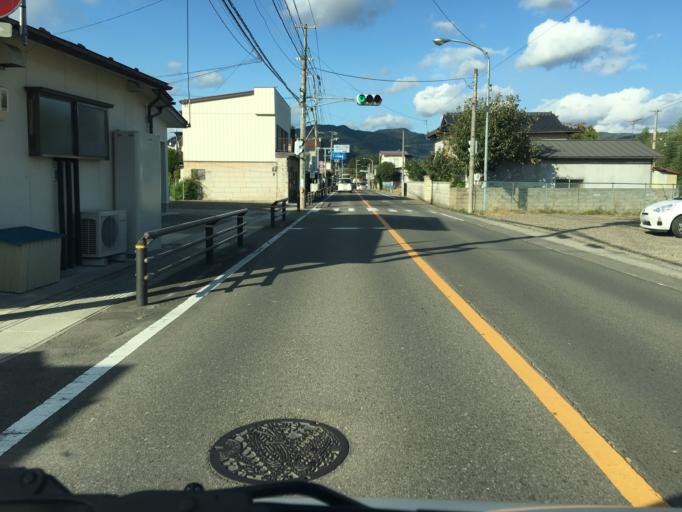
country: JP
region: Fukushima
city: Fukushima-shi
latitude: 37.8172
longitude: 140.4463
